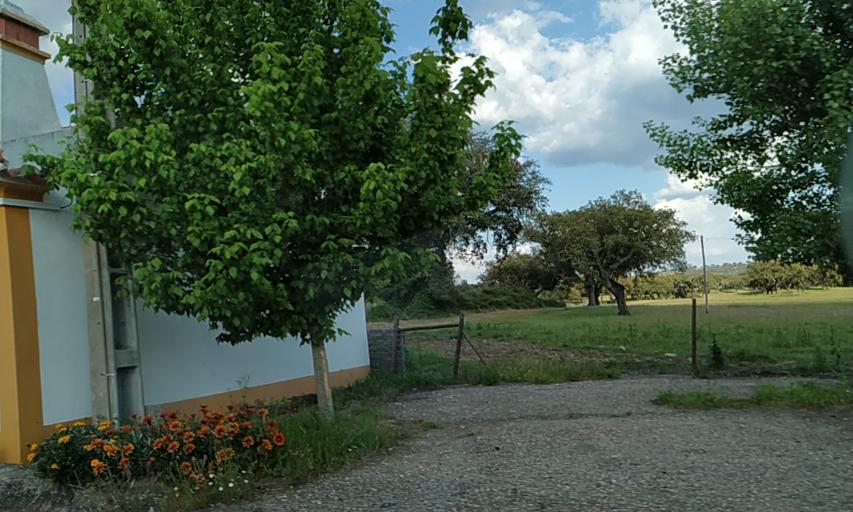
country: PT
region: Portalegre
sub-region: Portalegre
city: Urra
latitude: 39.2353
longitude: -7.4529
